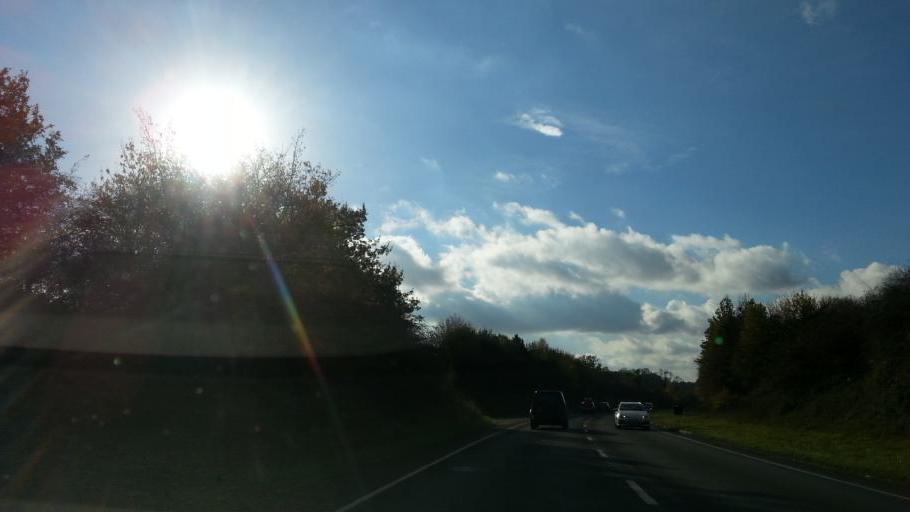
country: GB
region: England
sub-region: Norfolk
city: Harleston
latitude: 52.3765
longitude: 1.2513
